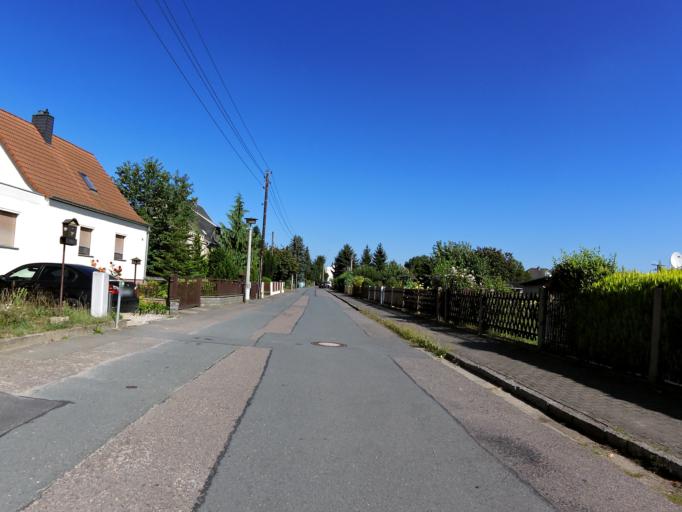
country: DE
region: Saxony
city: Riesa
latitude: 51.3300
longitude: 13.2959
